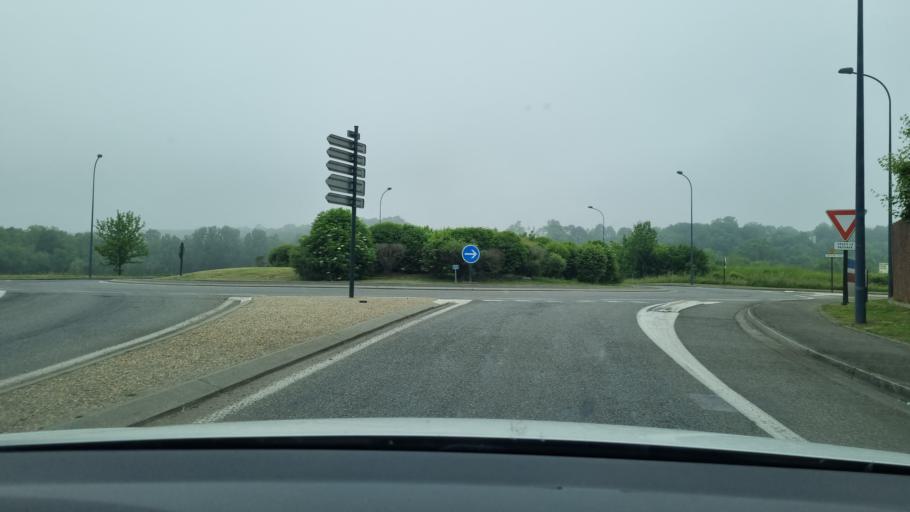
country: FR
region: Aquitaine
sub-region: Departement des Landes
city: Amou
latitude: 43.5458
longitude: -0.6830
